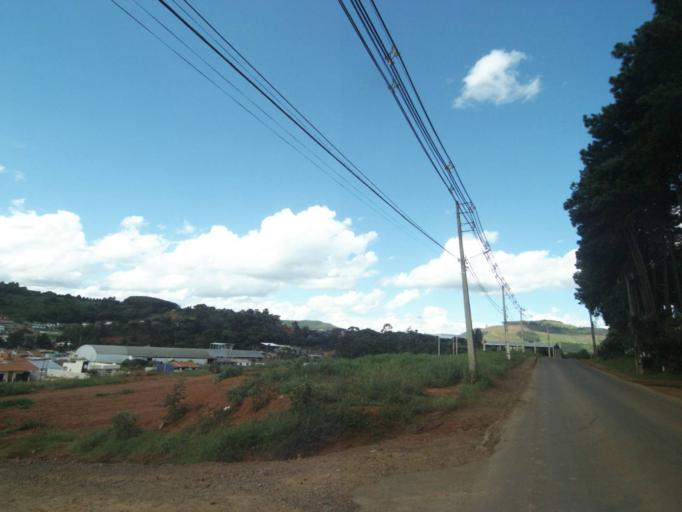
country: BR
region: Parana
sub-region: Uniao Da Vitoria
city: Uniao da Vitoria
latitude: -26.1526
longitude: -51.5414
